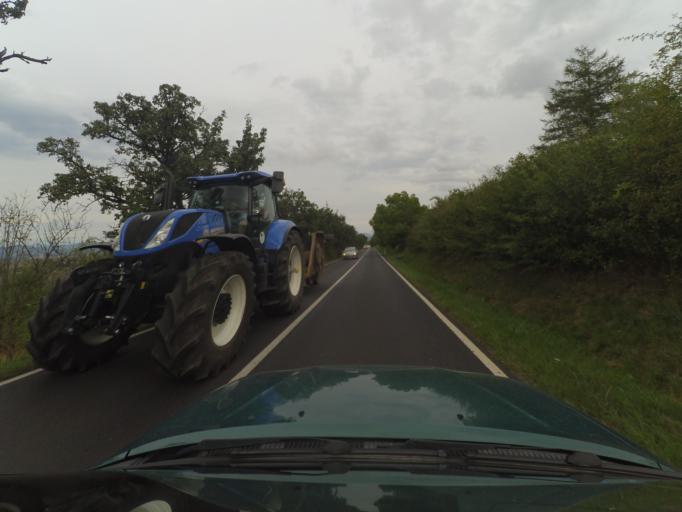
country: CZ
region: Ustecky
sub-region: Okres Louny
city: Louny
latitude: 50.3077
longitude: 13.7908
